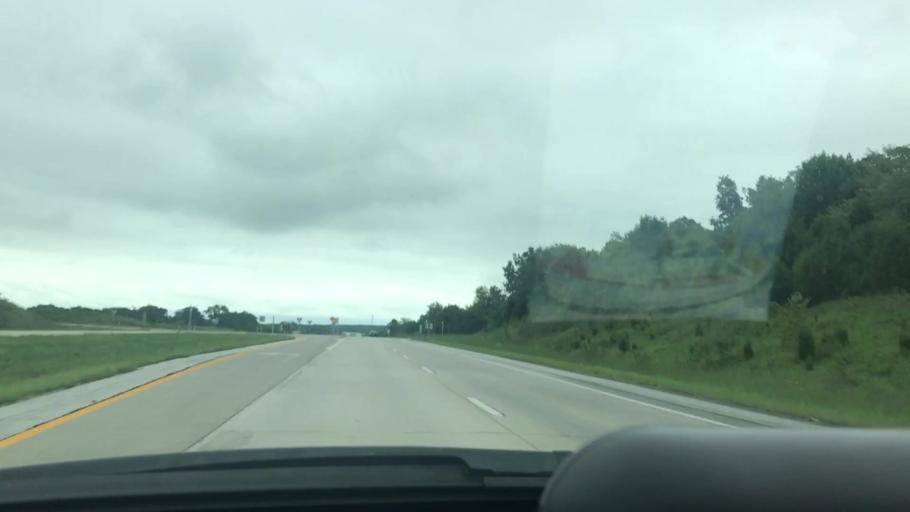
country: US
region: Missouri
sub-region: Greene County
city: Strafford
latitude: 37.2997
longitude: -93.1770
